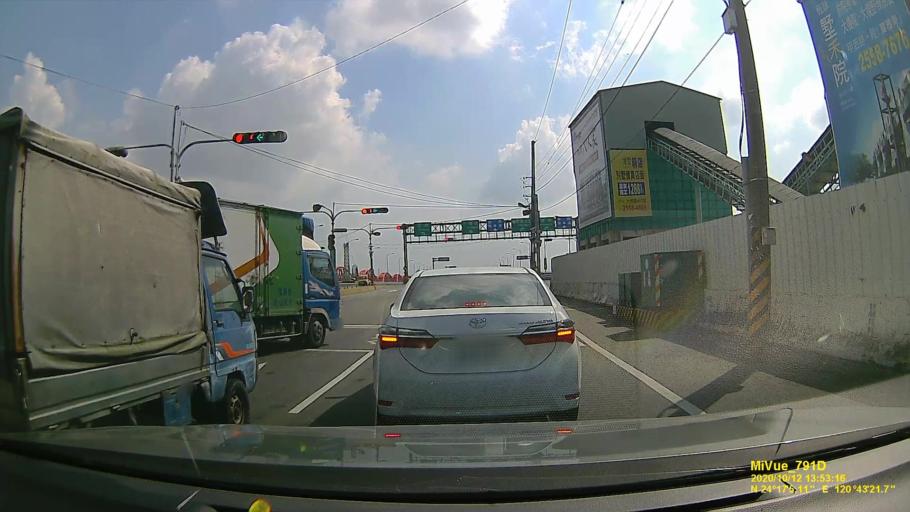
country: TW
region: Taiwan
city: Fengyuan
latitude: 24.2848
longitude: 120.7227
